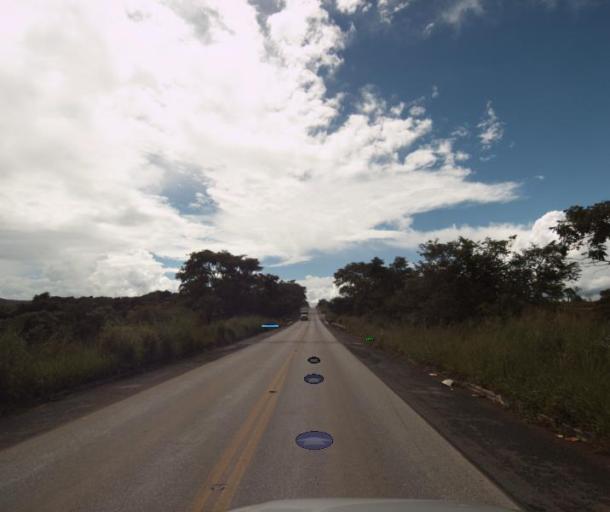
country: BR
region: Goias
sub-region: Uruacu
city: Uruacu
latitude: -14.1925
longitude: -49.1279
